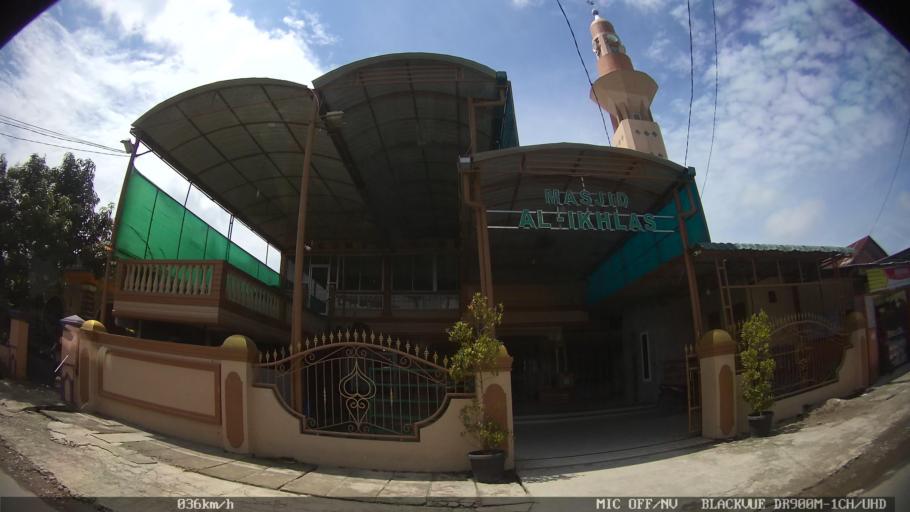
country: ID
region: North Sumatra
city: Percut
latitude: 3.6020
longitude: 98.7695
